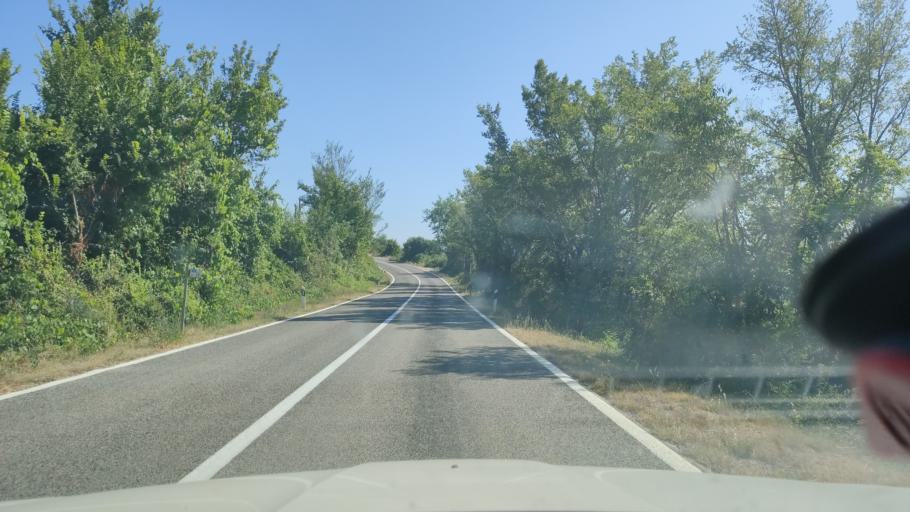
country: HR
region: Sibensko-Kniniska
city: Kistanje
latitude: 43.9579
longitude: 15.8623
